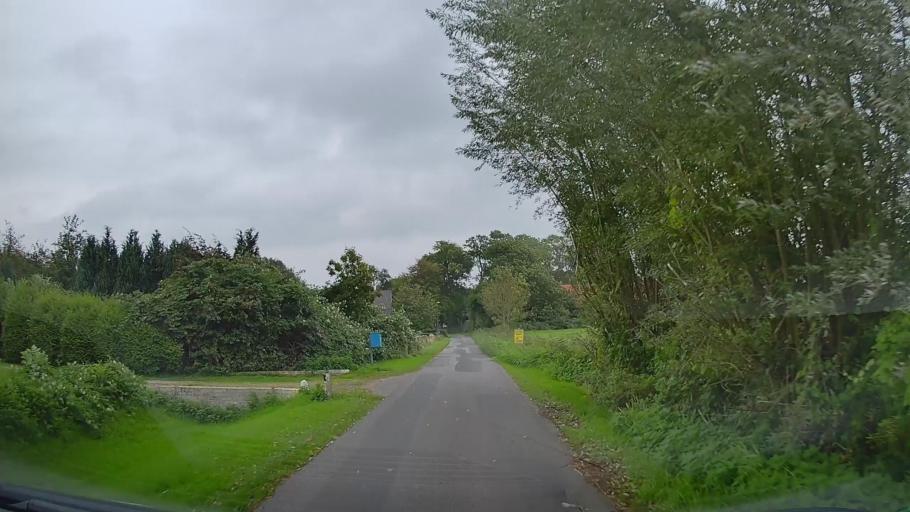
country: DE
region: Lower Saxony
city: Freiburg
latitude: 53.8272
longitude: 9.2638
